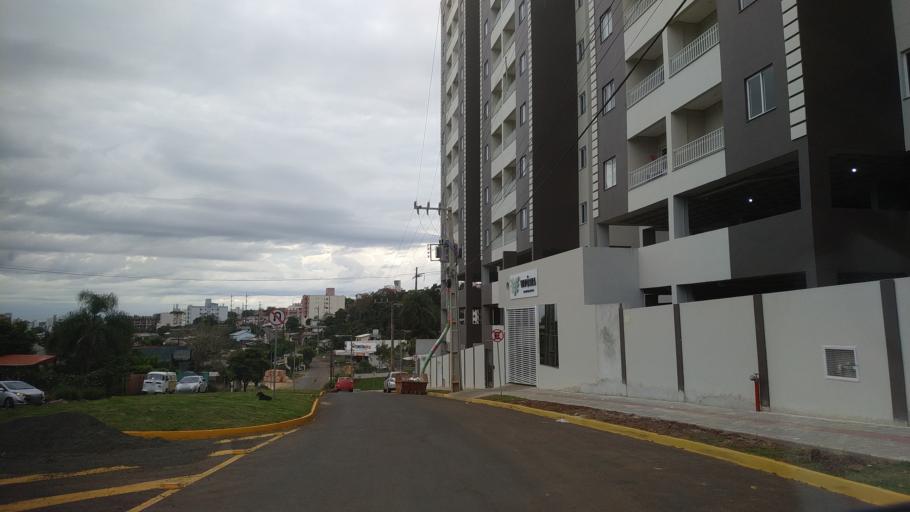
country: BR
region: Santa Catarina
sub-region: Chapeco
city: Chapeco
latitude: -27.0736
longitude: -52.6089
